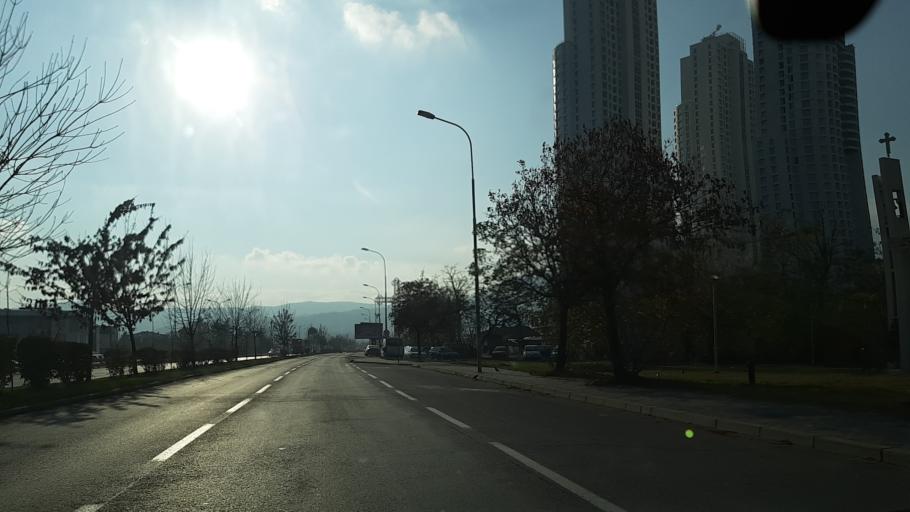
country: MK
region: Kisela Voda
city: Usje
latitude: 41.9812
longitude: 21.4696
